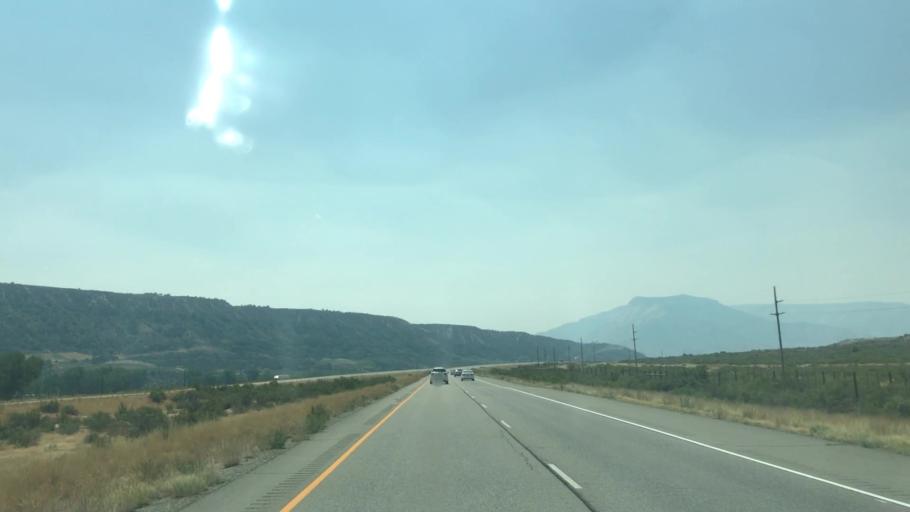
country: US
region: Colorado
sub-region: Garfield County
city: Battlement Mesa
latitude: 39.4817
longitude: -107.9692
